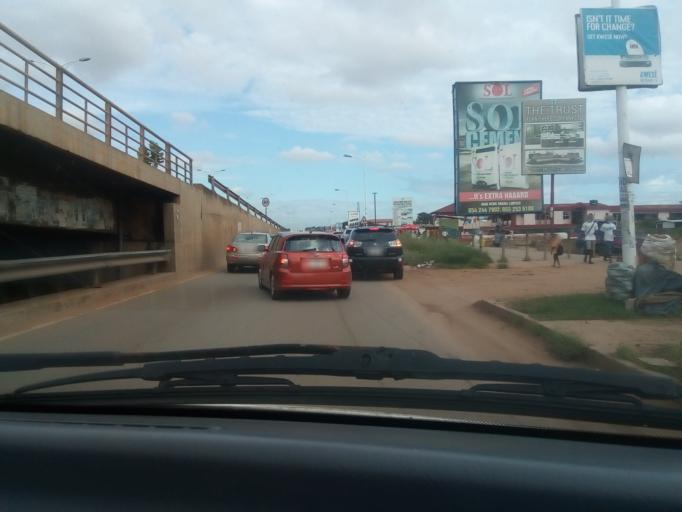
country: GH
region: Greater Accra
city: Dome
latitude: 5.6573
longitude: -0.2650
